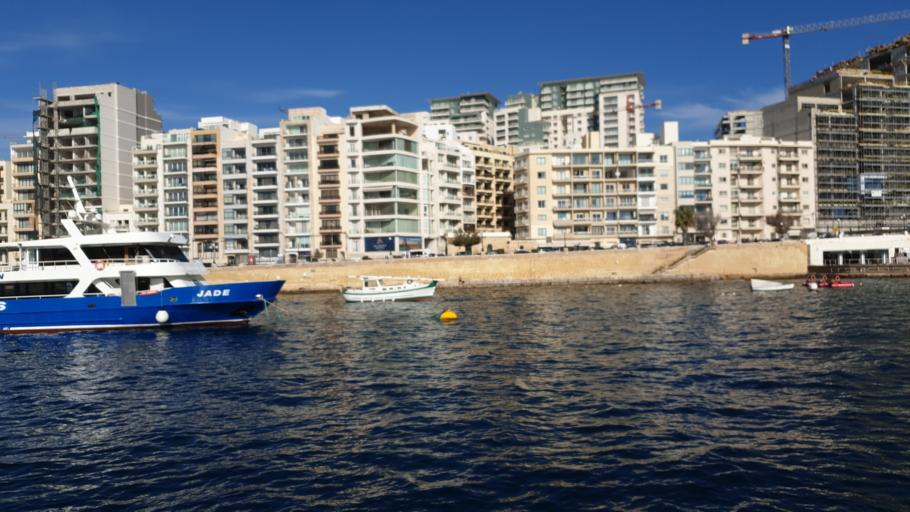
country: MT
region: Tas-Sliema
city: Sliema
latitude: 35.9060
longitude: 14.5075
